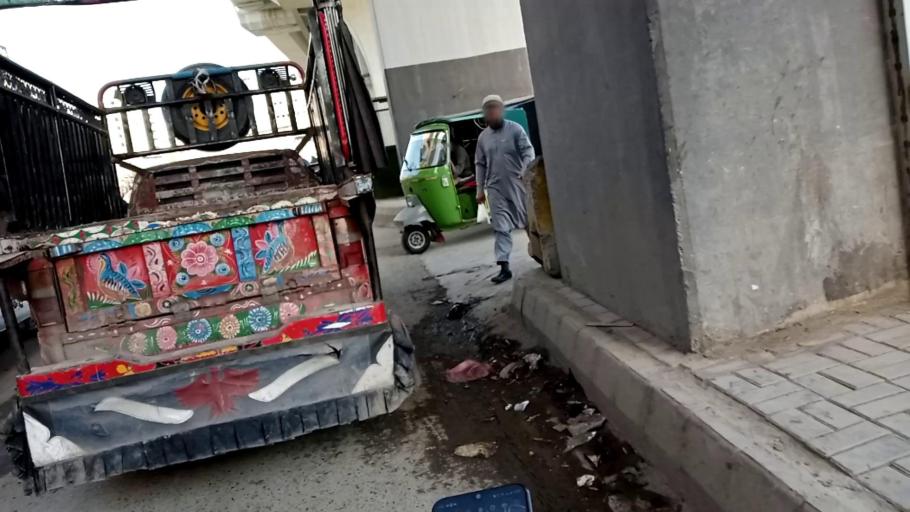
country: PK
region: Khyber Pakhtunkhwa
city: Peshawar
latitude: 34.0075
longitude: 71.5606
